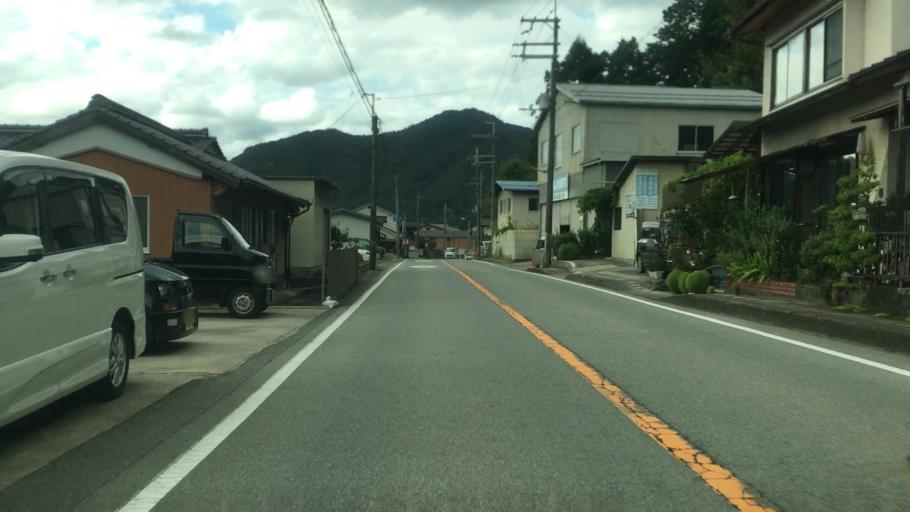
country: JP
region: Kyoto
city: Fukuchiyama
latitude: 35.3125
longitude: 134.8896
